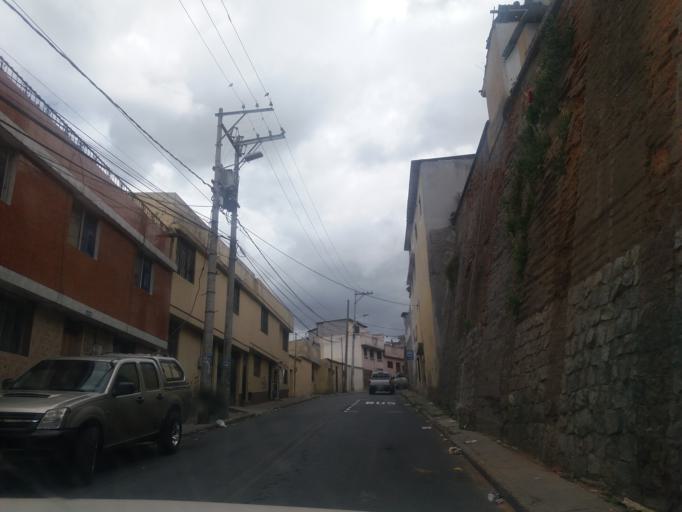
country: EC
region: Pichincha
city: Quito
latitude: -0.2215
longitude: -78.5245
